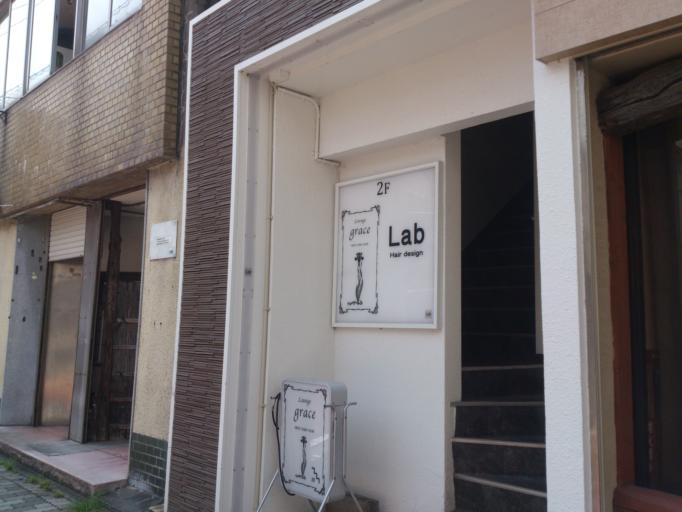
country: JP
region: Shizuoka
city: Shizuoka-shi
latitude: 34.9700
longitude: 138.3888
